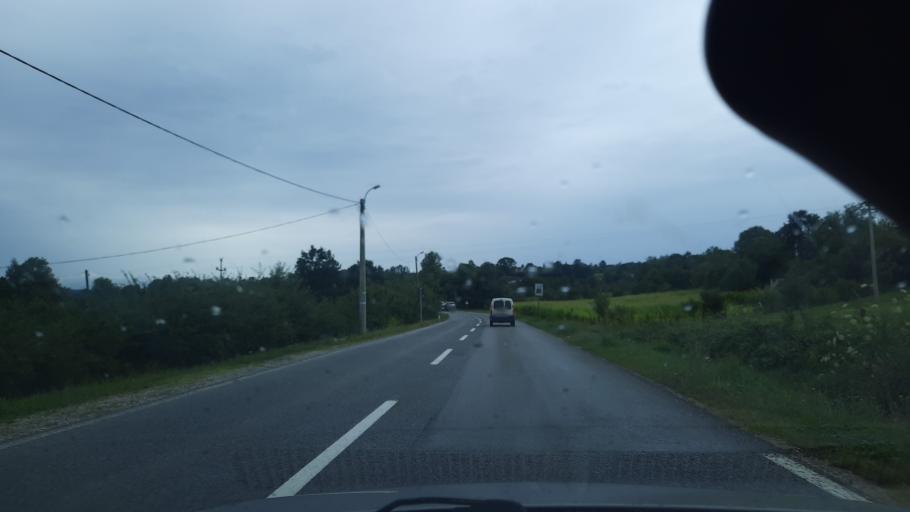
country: RS
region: Central Serbia
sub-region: Raski Okrug
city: Kraljevo
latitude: 43.7774
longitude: 20.7957
